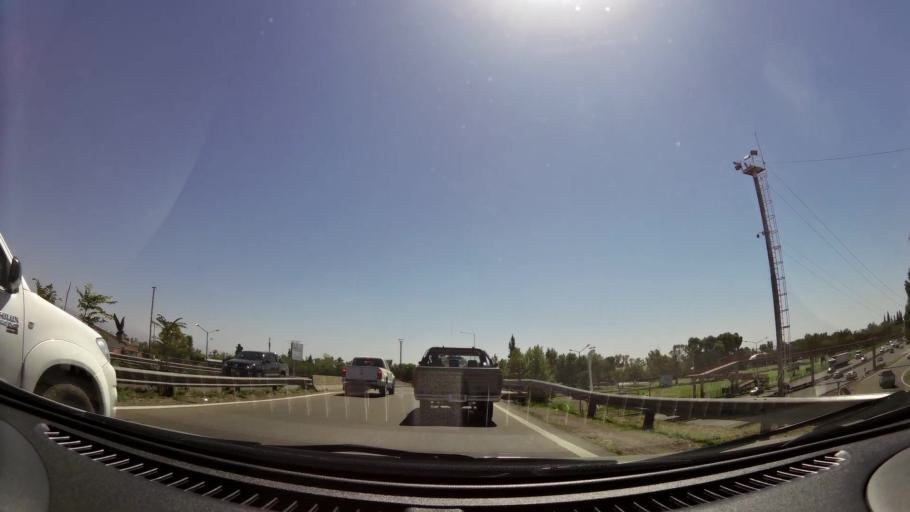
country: AR
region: Mendoza
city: Mendoza
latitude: -32.8983
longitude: -68.8191
